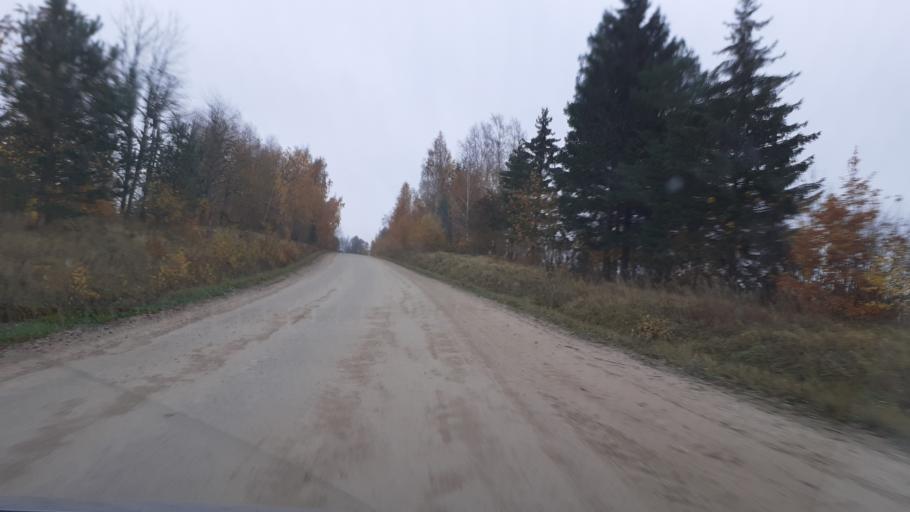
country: LV
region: Kuldigas Rajons
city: Kuldiga
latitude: 56.9412
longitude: 21.8232
